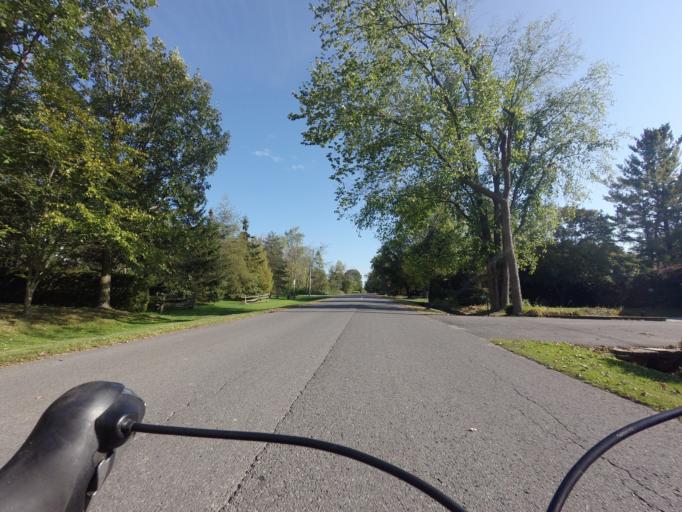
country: CA
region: Ontario
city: Bells Corners
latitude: 45.2261
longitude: -75.6764
